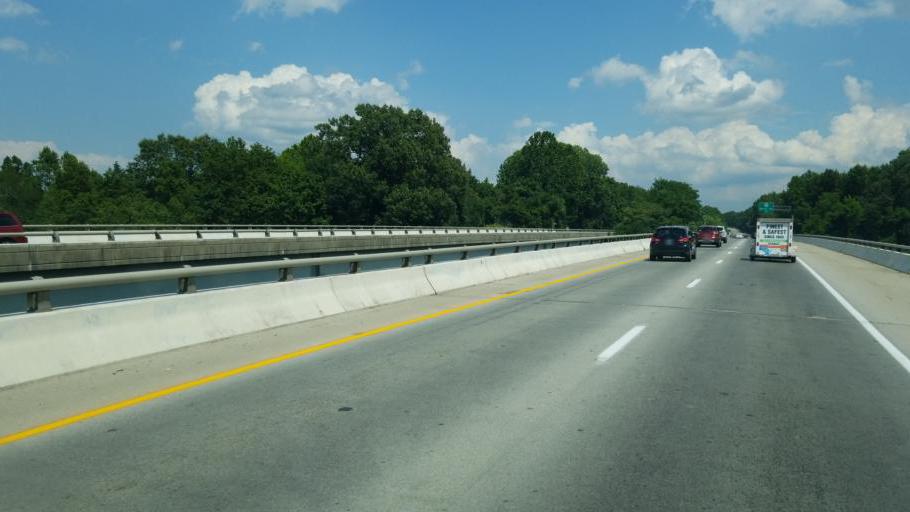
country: US
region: Virginia
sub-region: City of Suffolk
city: Suffolk
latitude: 36.7647
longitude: -76.5613
